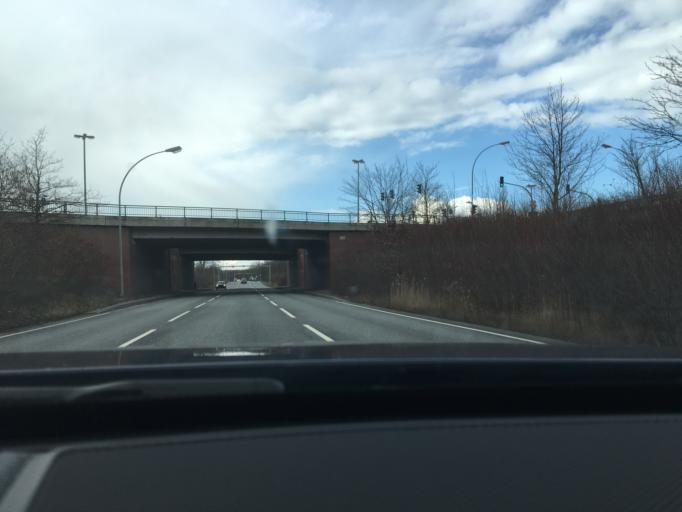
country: DE
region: Bremen
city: Bremerhaven
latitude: 53.5504
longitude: 8.5951
